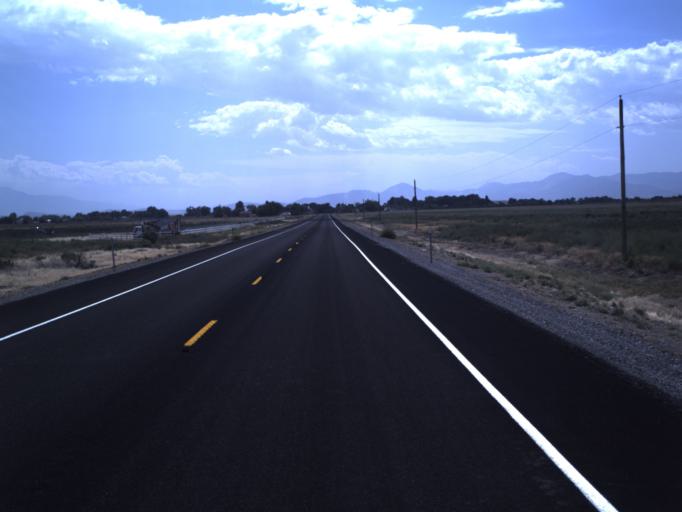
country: US
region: Utah
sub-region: Utah County
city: Eagle Mountain
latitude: 40.2776
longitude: -112.0949
